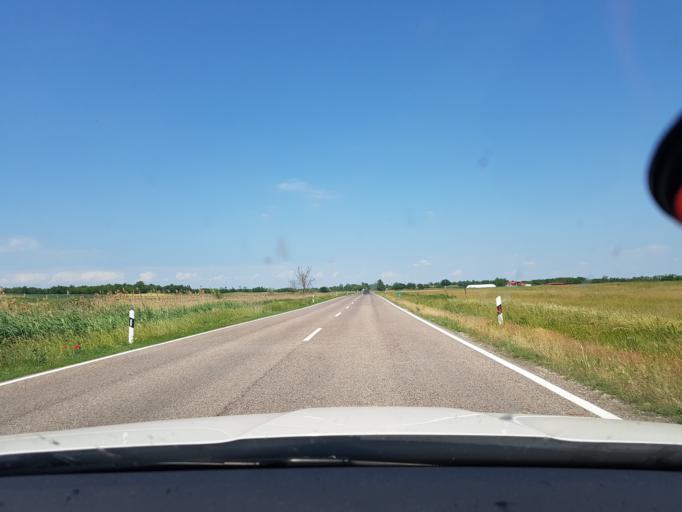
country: HU
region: Hajdu-Bihar
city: Egyek
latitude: 47.5809
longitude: 20.8542
